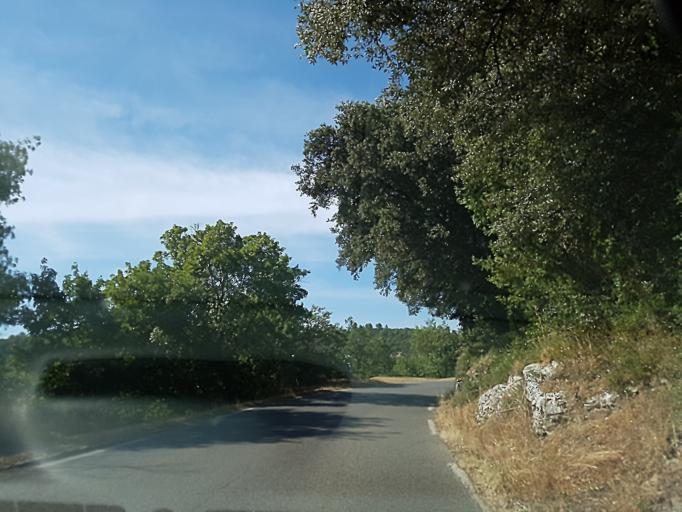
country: FR
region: Provence-Alpes-Cote d'Azur
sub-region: Departement du Var
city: Bras
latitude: 43.4688
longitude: 5.9468
